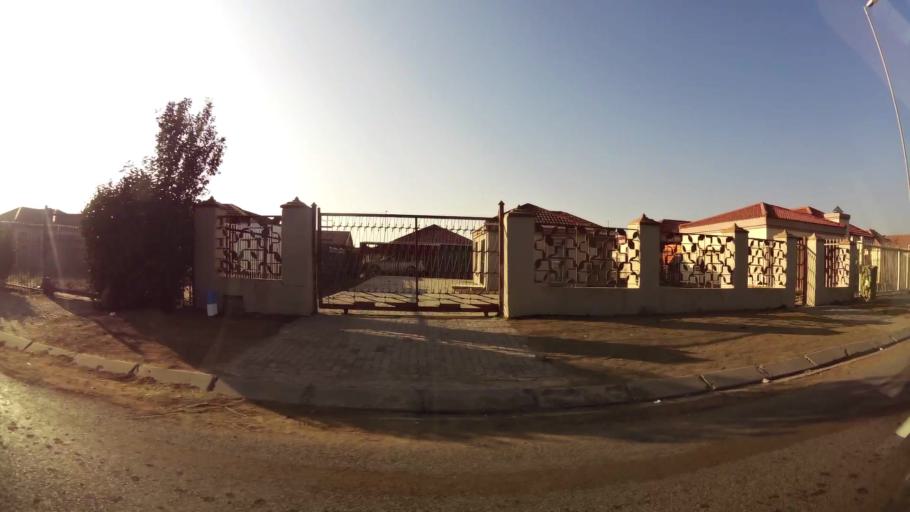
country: ZA
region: Orange Free State
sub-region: Mangaung Metropolitan Municipality
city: Bloemfontein
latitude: -29.1540
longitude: 26.2100
